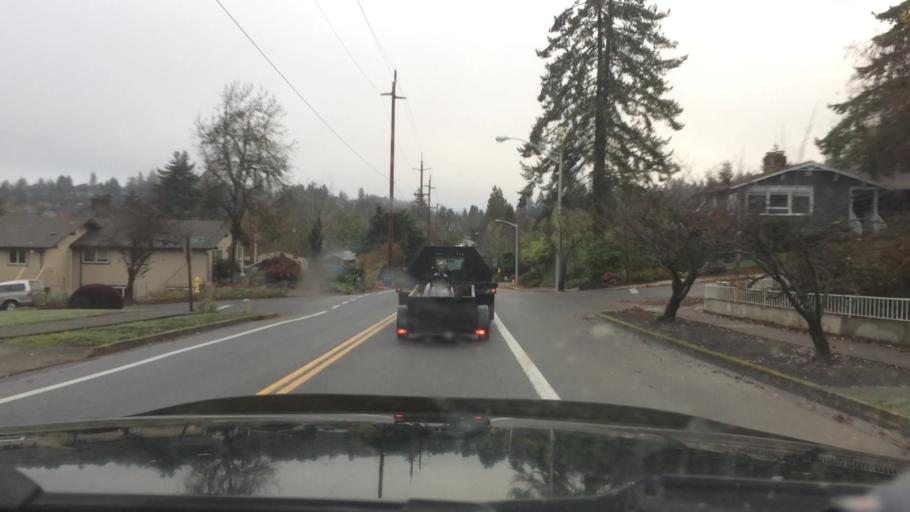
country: US
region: Oregon
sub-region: Lane County
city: Eugene
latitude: 44.0277
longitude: -123.1137
